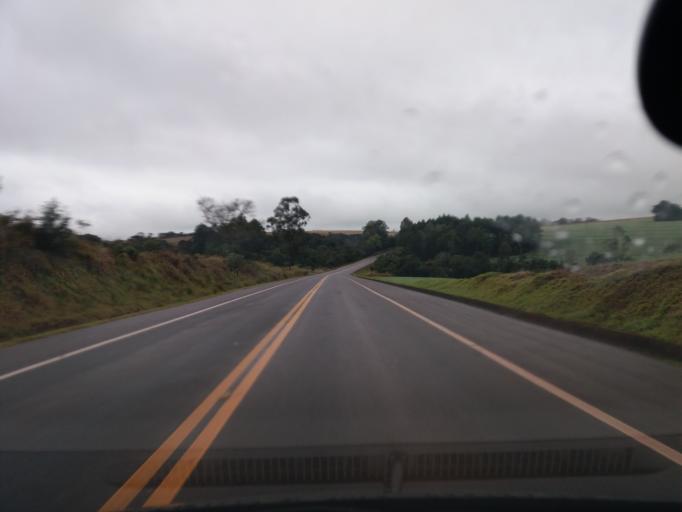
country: BR
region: Parana
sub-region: Campo Mourao
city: Campo Mourao
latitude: -24.3227
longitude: -52.6456
